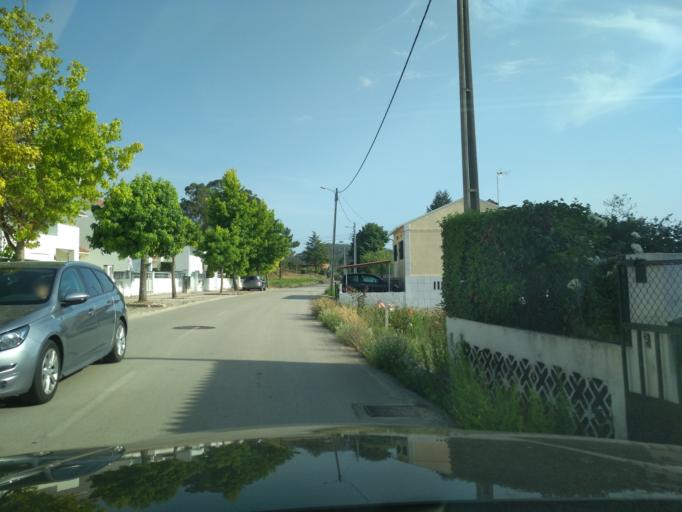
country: PT
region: Coimbra
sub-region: Condeixa-A-Nova
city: Condeixa-a-Nova
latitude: 40.1360
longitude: -8.4677
